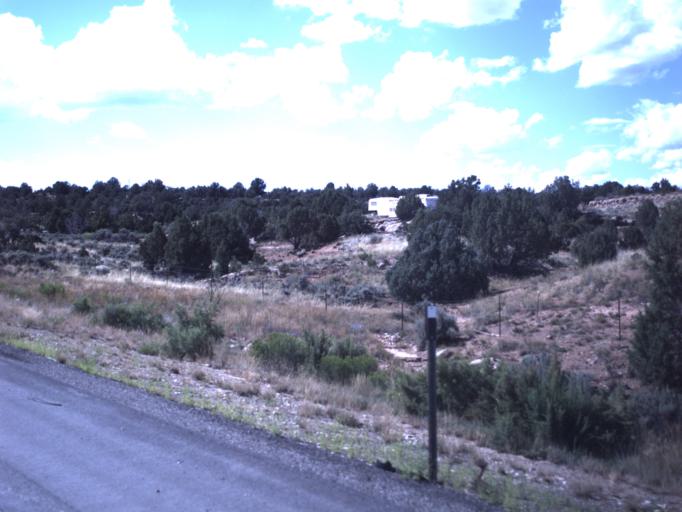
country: US
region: Utah
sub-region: Duchesne County
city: Duchesne
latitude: 40.2031
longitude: -110.7908
